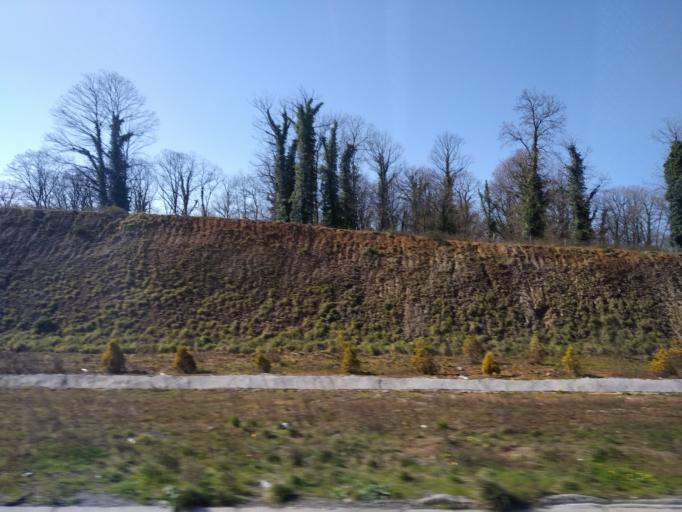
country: TR
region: Istanbul
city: Sancaktepe
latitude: 41.0633
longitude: 29.2752
